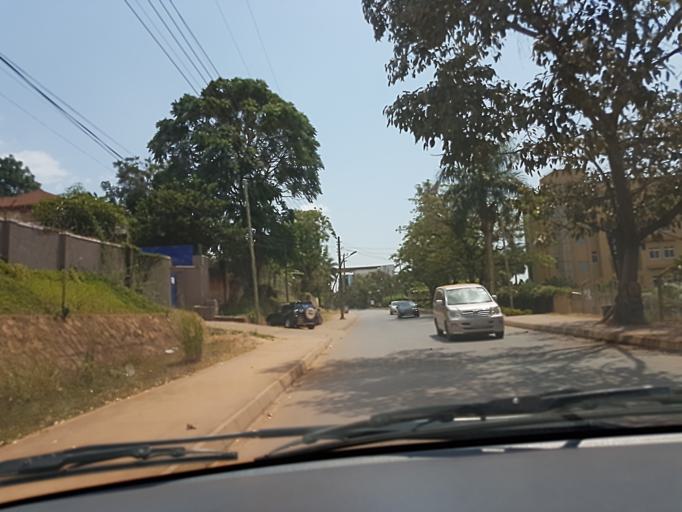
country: UG
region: Central Region
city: Kampala Central Division
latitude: 0.3248
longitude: 32.5771
